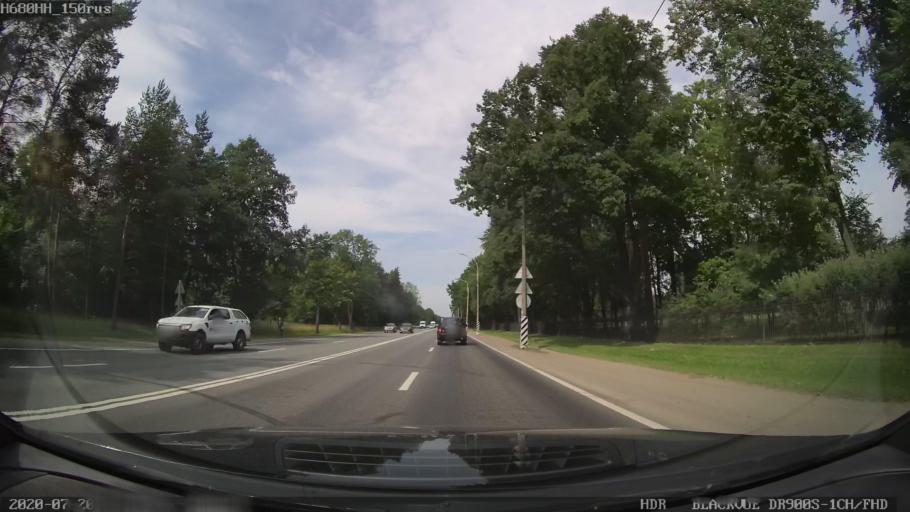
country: RU
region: Leningrad
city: Ol'gino
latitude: 59.8752
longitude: 29.9430
